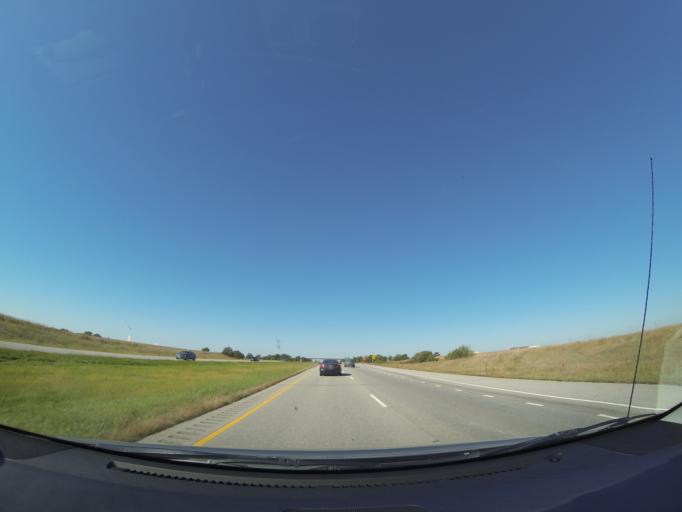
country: US
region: Nebraska
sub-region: Seward County
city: Milford
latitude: 40.8223
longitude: -97.0955
